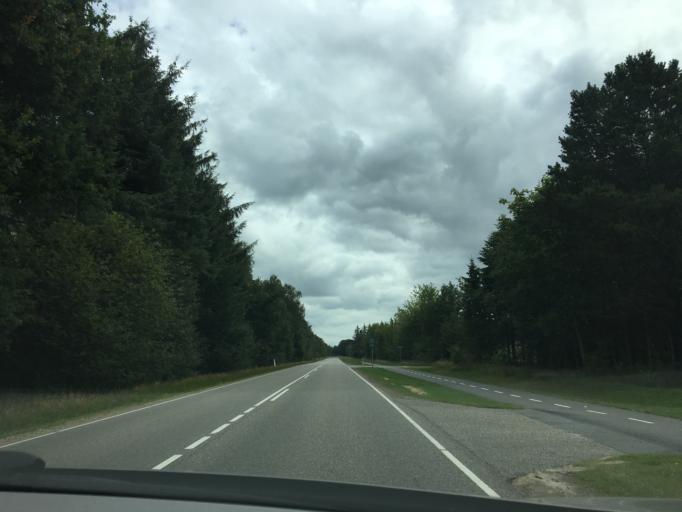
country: DK
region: South Denmark
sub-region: Billund Kommune
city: Grindsted
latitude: 55.8214
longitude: 9.0022
